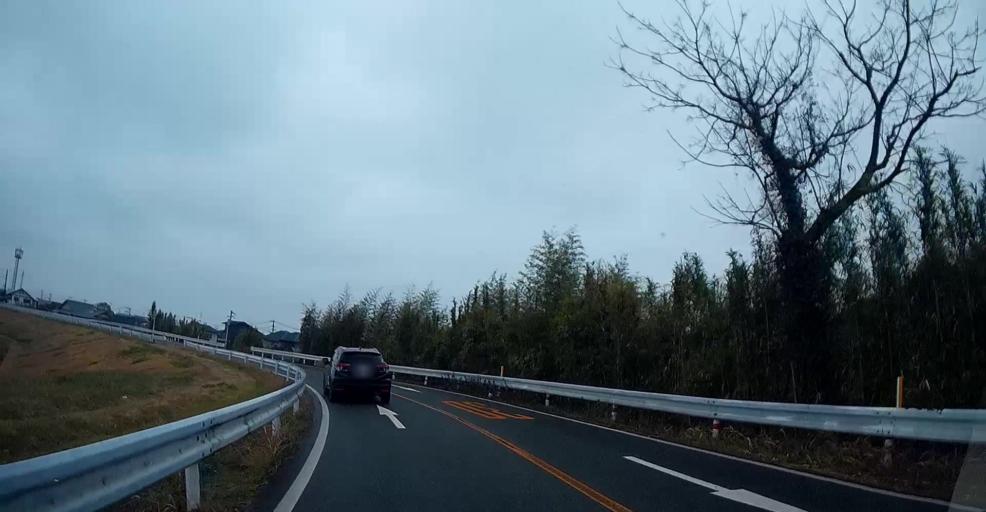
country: JP
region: Kumamoto
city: Kumamoto
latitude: 32.7546
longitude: 130.7410
